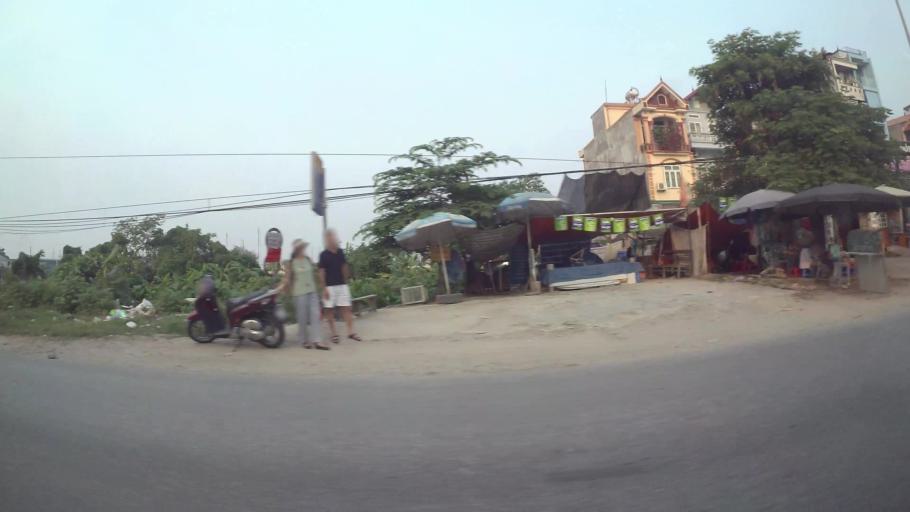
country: VN
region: Ha Noi
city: Thuong Tin
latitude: 20.8760
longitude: 105.8625
